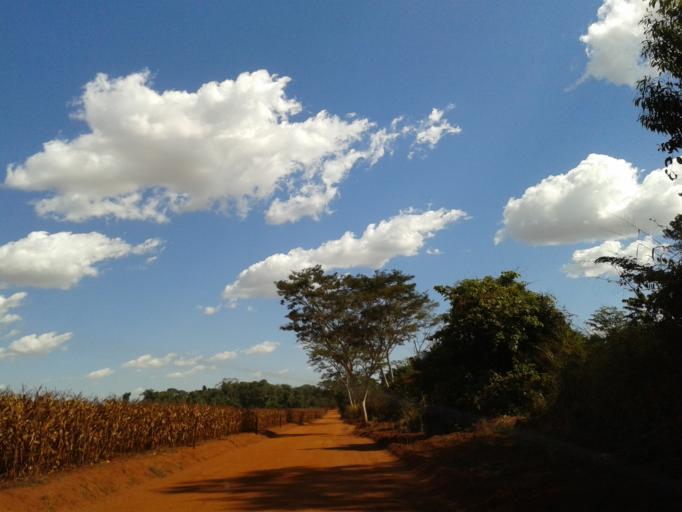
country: BR
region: Minas Gerais
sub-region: Capinopolis
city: Capinopolis
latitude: -18.6193
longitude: -49.4808
